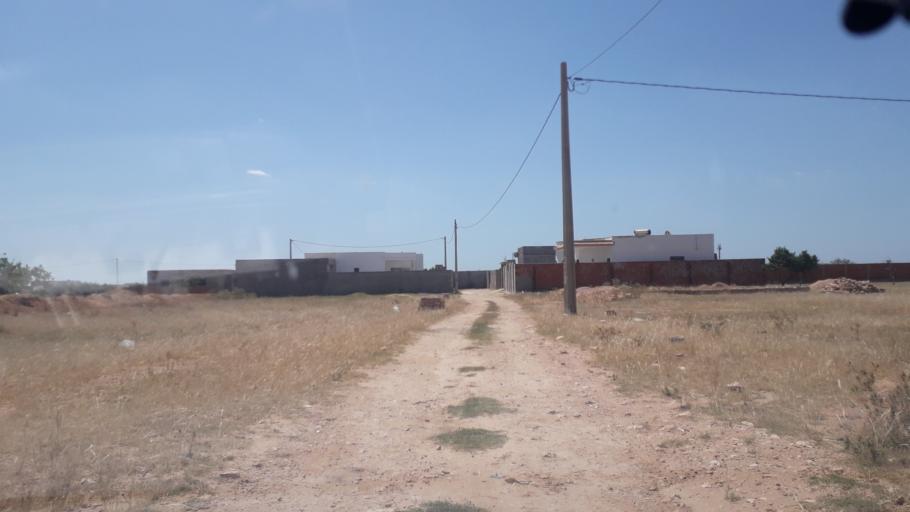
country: TN
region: Safaqis
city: Al Qarmadah
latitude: 34.8357
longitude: 10.7745
